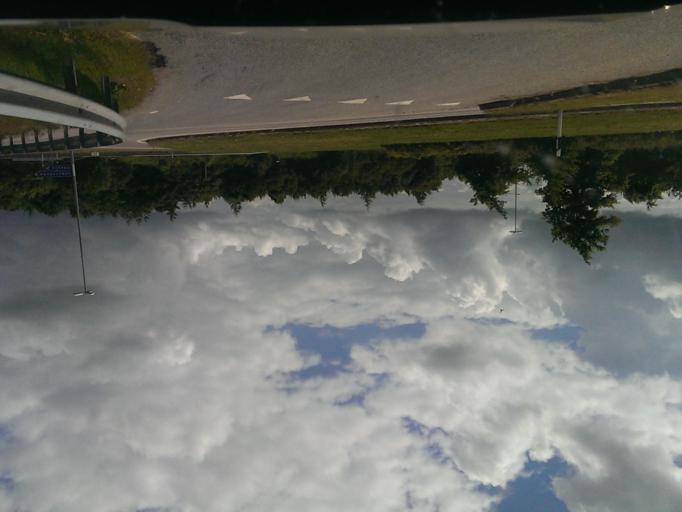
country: SE
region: Skane
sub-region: Eslovs Kommun
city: Eslov
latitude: 55.8560
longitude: 13.3055
